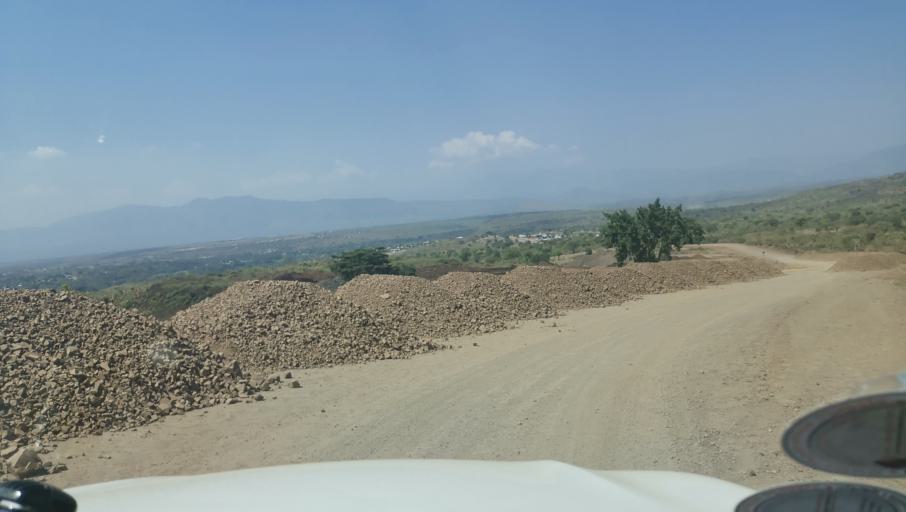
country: ET
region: Southern Nations, Nationalities, and People's Region
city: Arba Minch'
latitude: 6.3351
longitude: 37.3284
